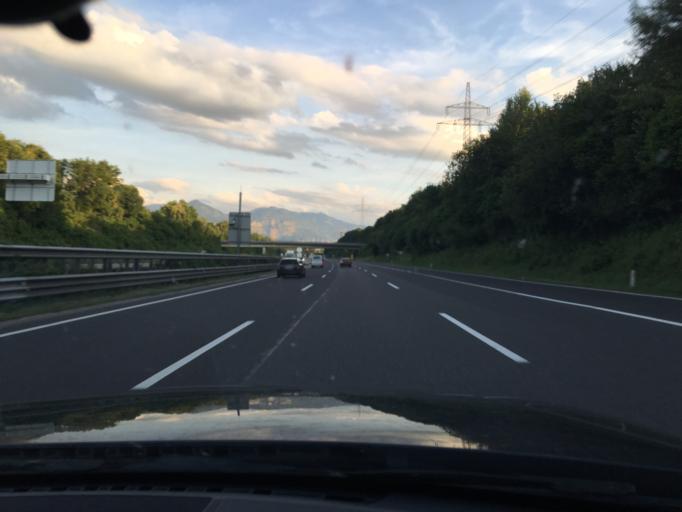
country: AT
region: Vorarlberg
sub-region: Politischer Bezirk Bregenz
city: Lauterach
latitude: 47.4806
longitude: 9.7407
